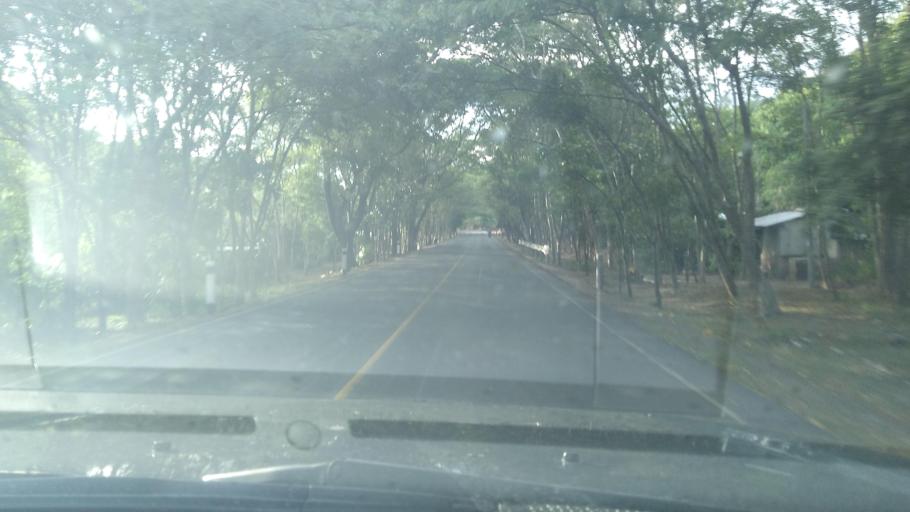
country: NI
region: Madriz
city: Yalaguina
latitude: 13.4754
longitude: -86.4806
